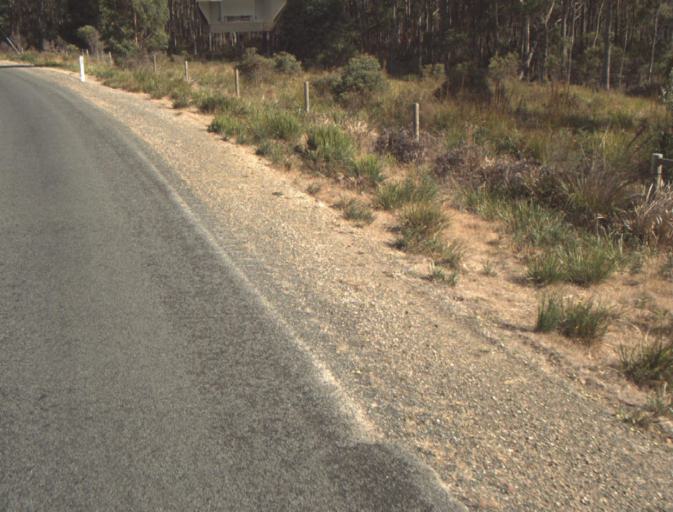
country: AU
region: Tasmania
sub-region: Dorset
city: Bridport
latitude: -41.1347
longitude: 147.2223
